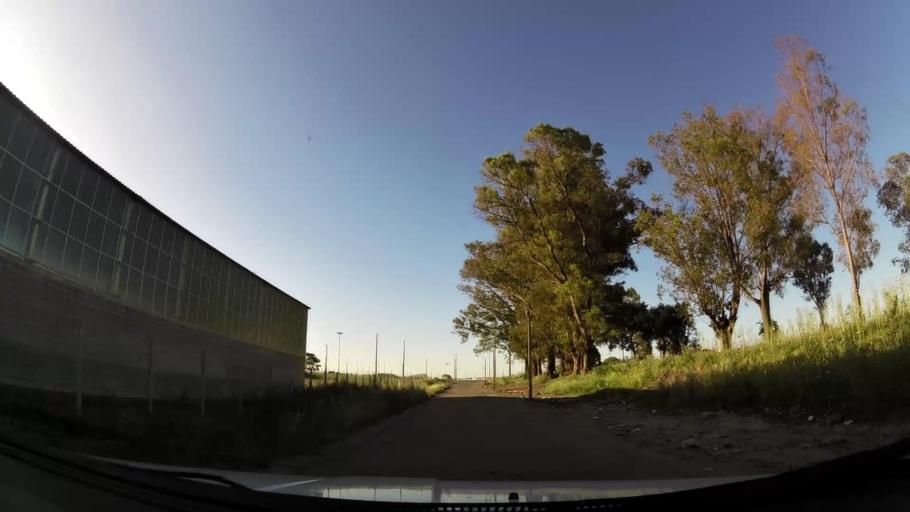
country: UY
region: Canelones
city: La Paz
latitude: -34.8276
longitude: -56.2460
